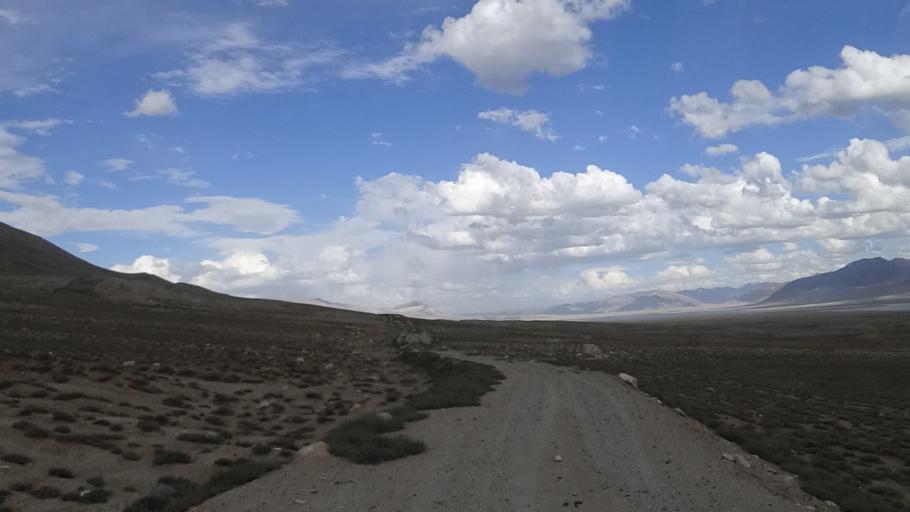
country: TJ
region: Gorno-Badakhshan
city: Murghob
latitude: 37.4686
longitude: 73.5789
